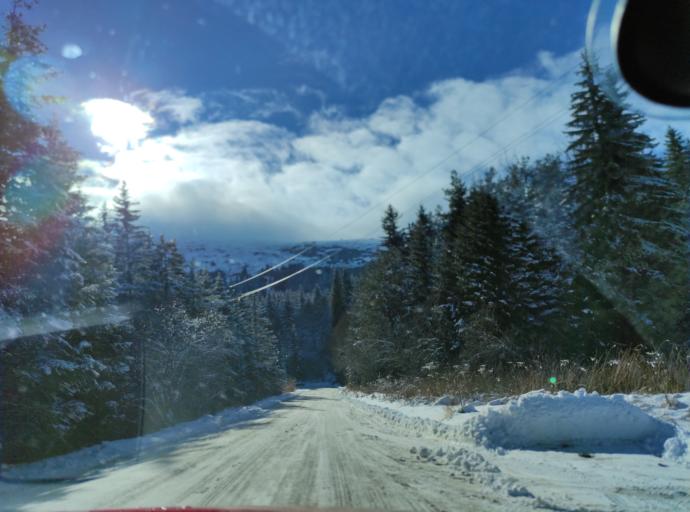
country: BG
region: Sofia-Capital
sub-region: Stolichna Obshtina
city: Sofia
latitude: 42.5891
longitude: 23.2975
